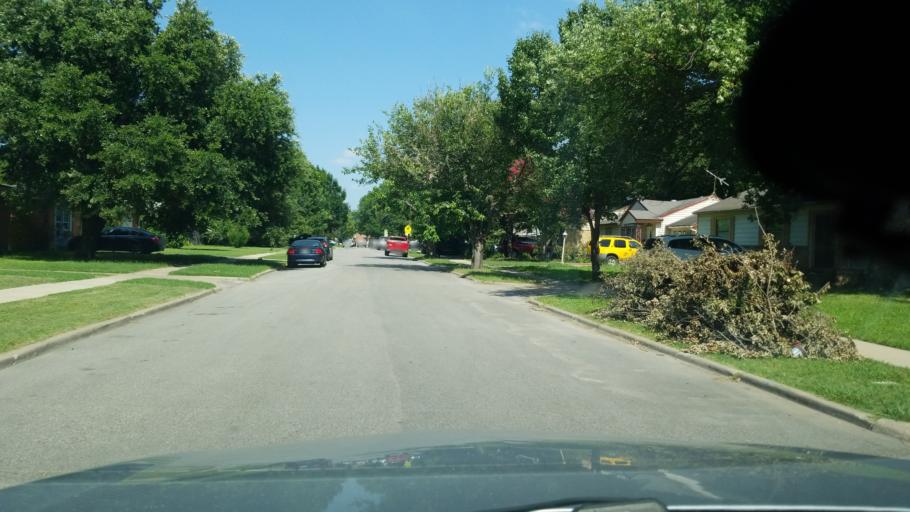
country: US
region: Texas
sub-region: Dallas County
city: Irving
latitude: 32.8131
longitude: -96.9627
